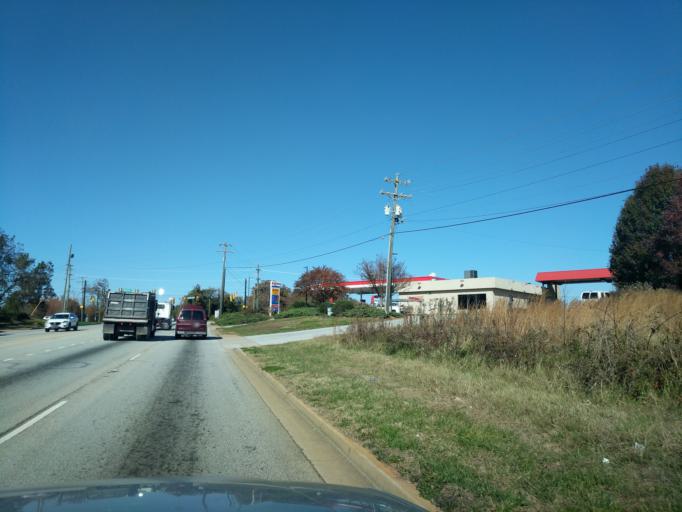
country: US
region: South Carolina
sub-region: Greenville County
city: Greer
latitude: 34.9260
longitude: -82.2443
